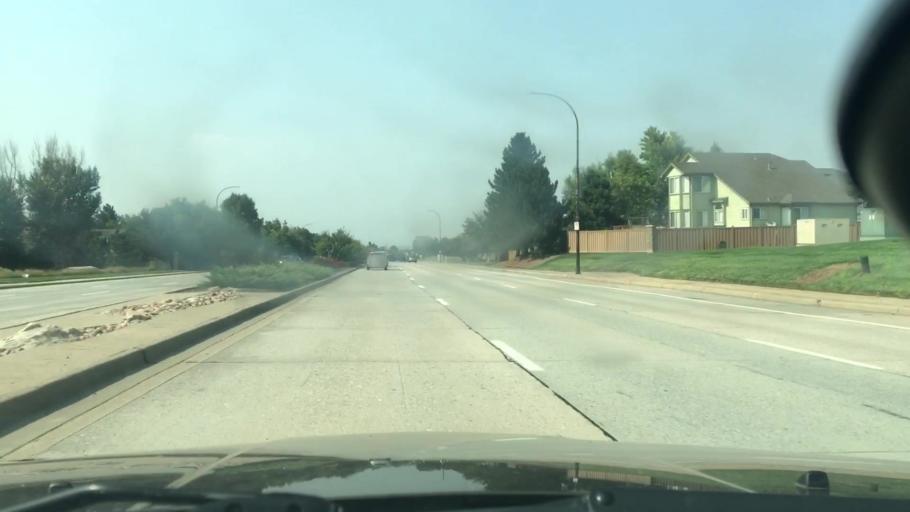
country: US
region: Colorado
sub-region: Douglas County
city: Acres Green
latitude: 39.5506
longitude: -104.9108
